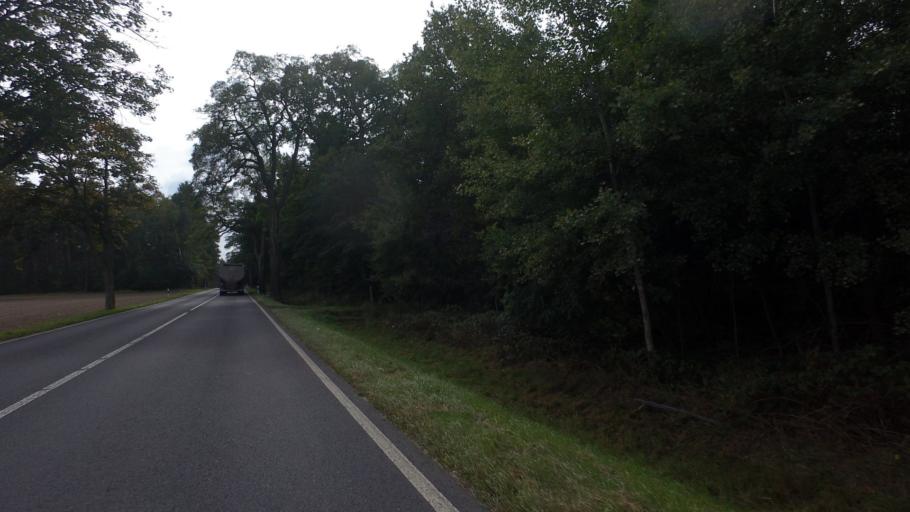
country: DE
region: Brandenburg
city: Kasel-Golzig
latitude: 51.8932
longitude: 13.6845
